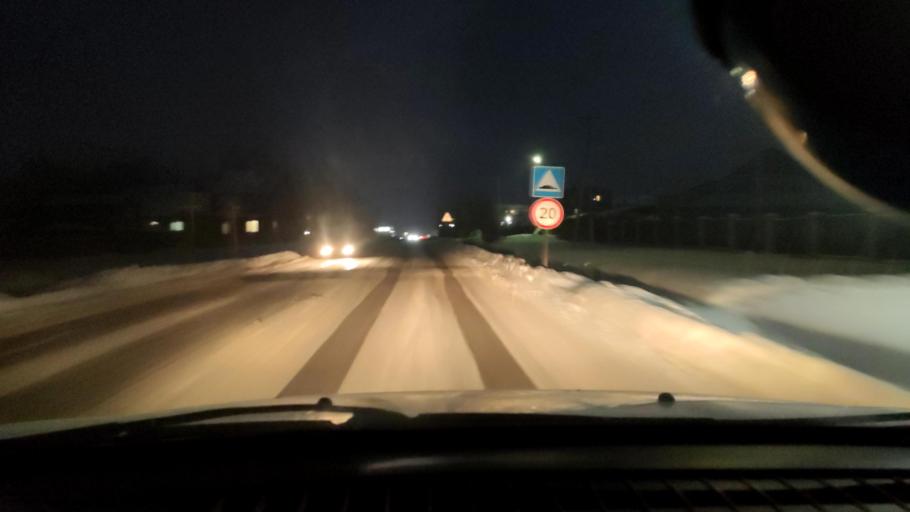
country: RU
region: Perm
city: Kultayevo
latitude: 57.8983
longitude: 55.9282
